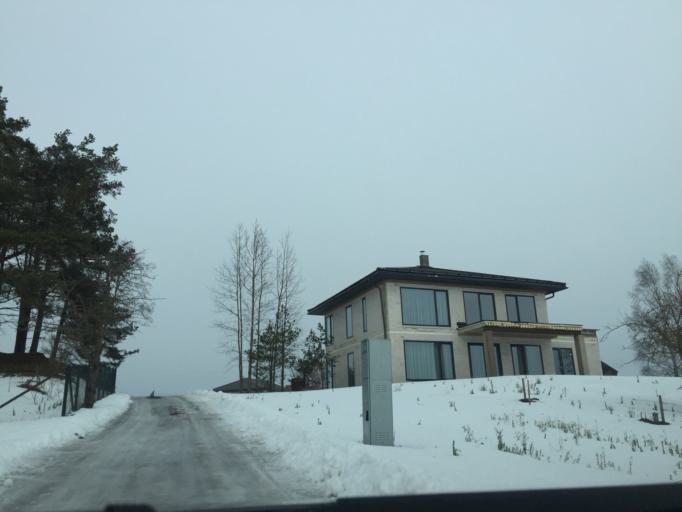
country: LV
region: Ikskile
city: Ikskile
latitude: 56.8437
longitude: 24.4590
